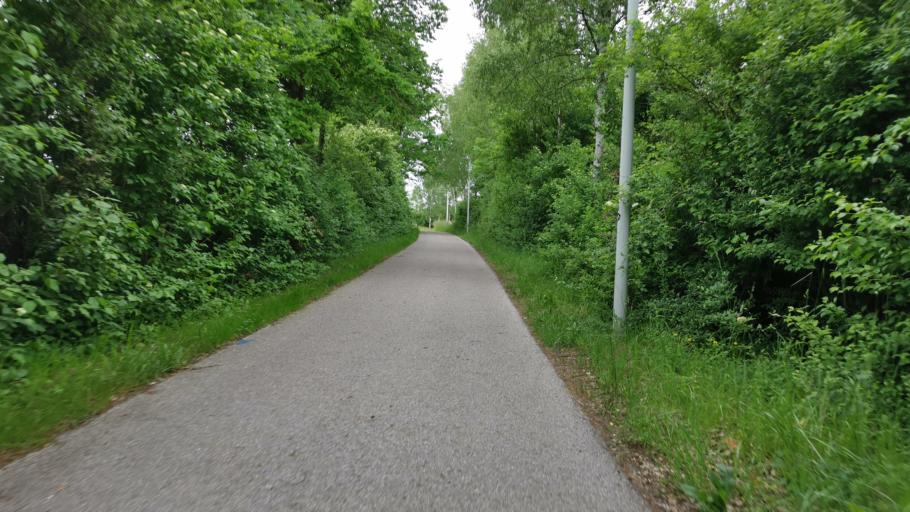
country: DE
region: Bavaria
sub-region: Upper Bavaria
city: Grafelfing
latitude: 48.1032
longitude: 11.4433
